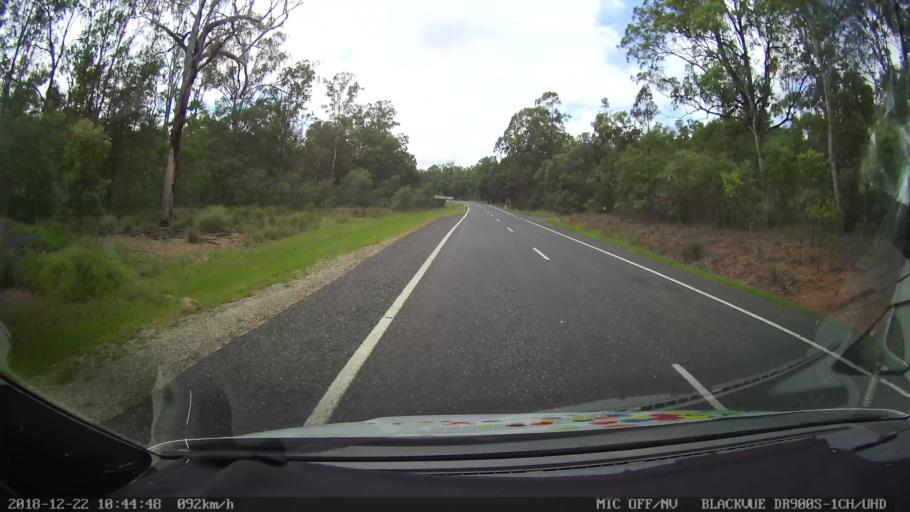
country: AU
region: New South Wales
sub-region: Clarence Valley
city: South Grafton
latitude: -29.6559
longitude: 152.8024
